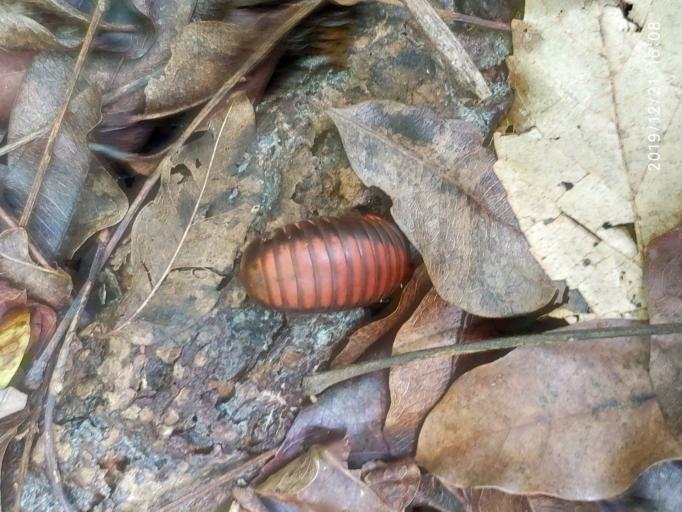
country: MG
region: Diana
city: Ambilobe
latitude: -12.9409
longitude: 49.1208
